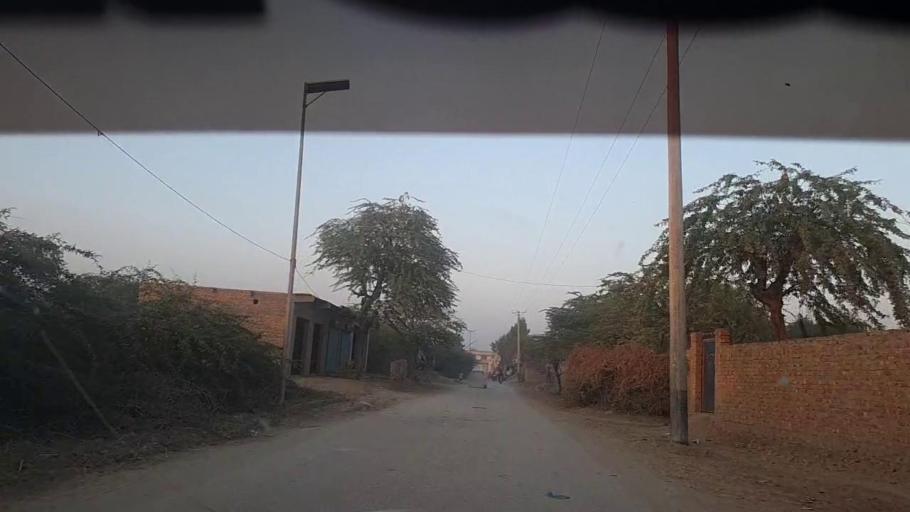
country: PK
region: Sindh
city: Ranipur
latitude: 27.2785
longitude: 68.5150
